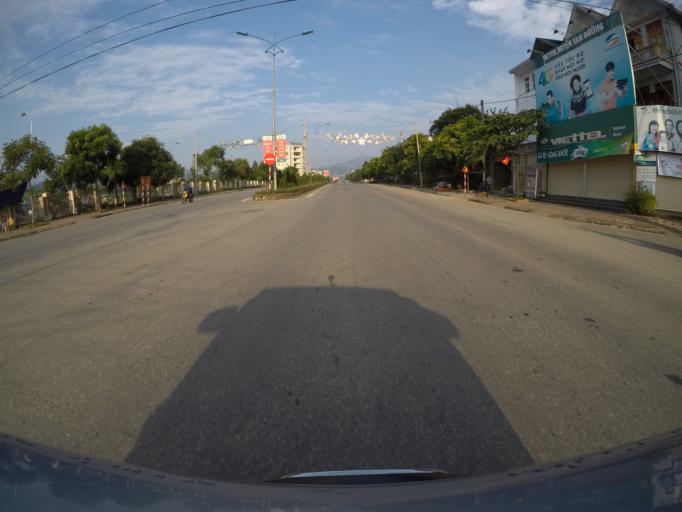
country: VN
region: Lai Chau
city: Tam Duong
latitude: 22.3214
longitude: 103.6242
